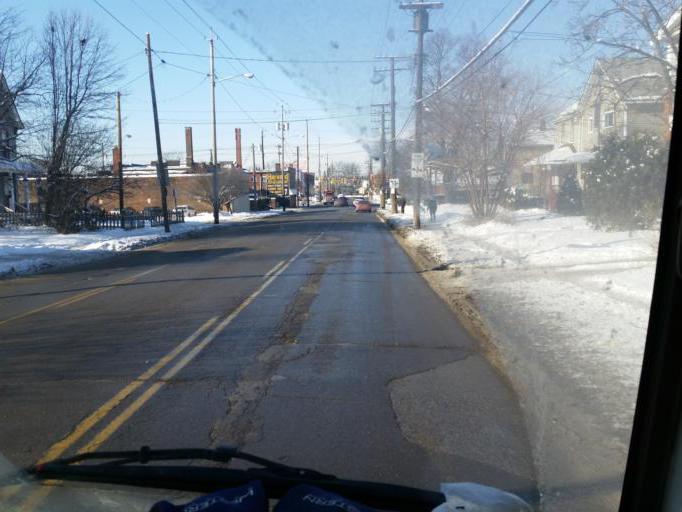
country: US
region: Ohio
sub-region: Cuyahoga County
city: Newburgh Heights
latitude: 41.4488
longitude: -81.6370
